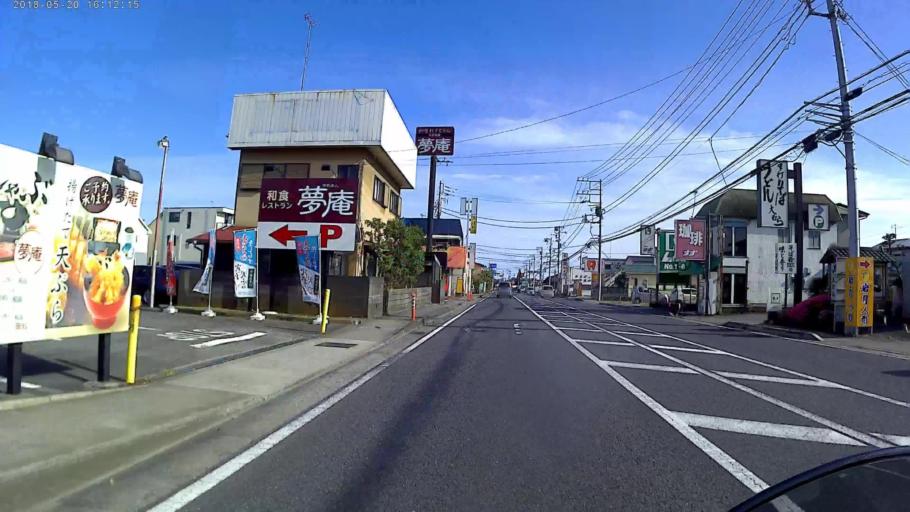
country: JP
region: Kanagawa
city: Odawara
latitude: 35.3222
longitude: 139.1588
